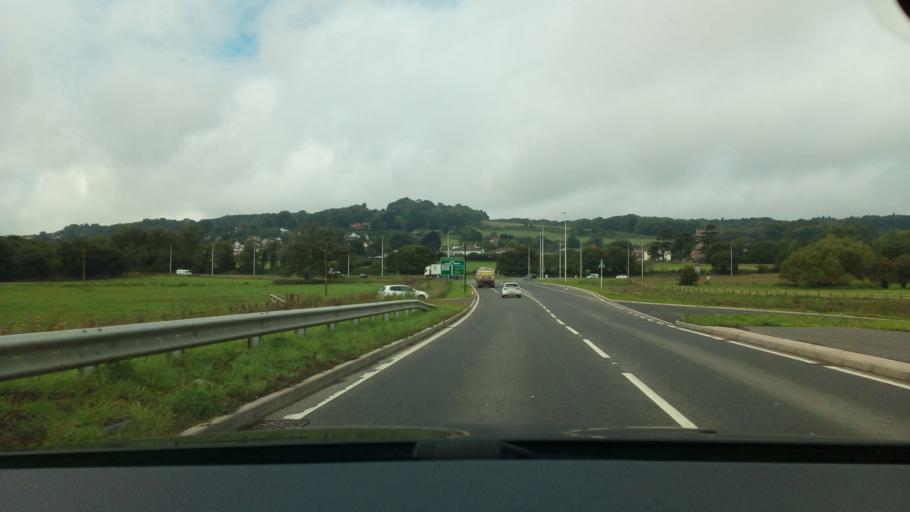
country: GB
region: England
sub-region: North Somerset
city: Long Ashton
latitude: 51.4325
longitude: -2.6385
